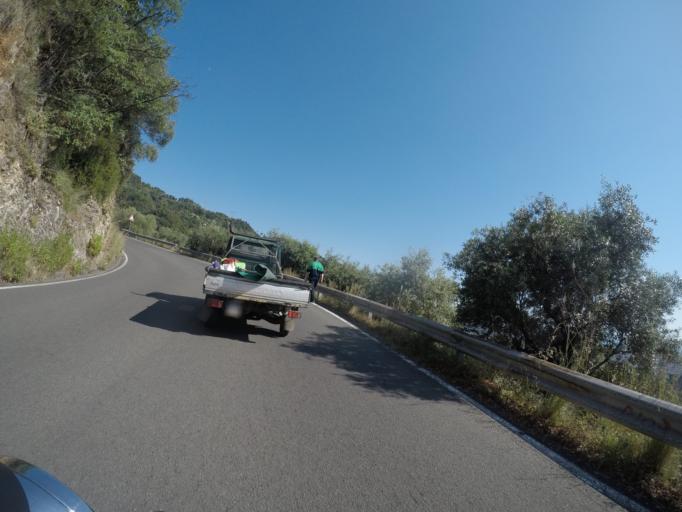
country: IT
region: Tuscany
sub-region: Provincia di Massa-Carrara
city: Montignoso
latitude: 44.0361
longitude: 10.1498
